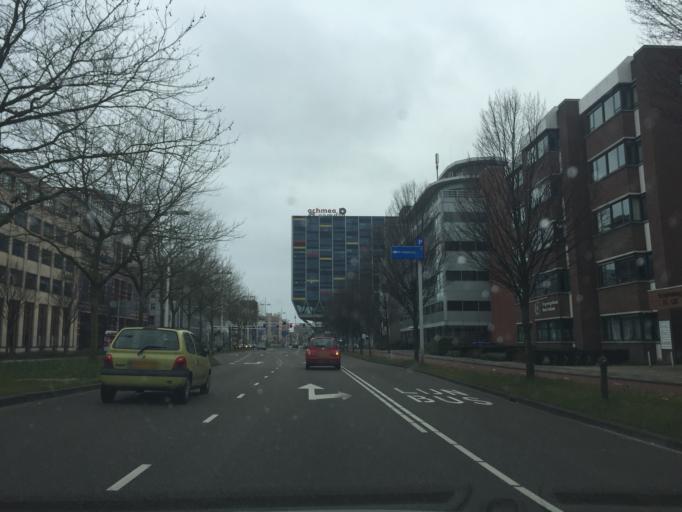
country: NL
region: South Holland
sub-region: Gemeente Leiden
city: Leiden
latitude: 52.1695
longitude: 4.4876
